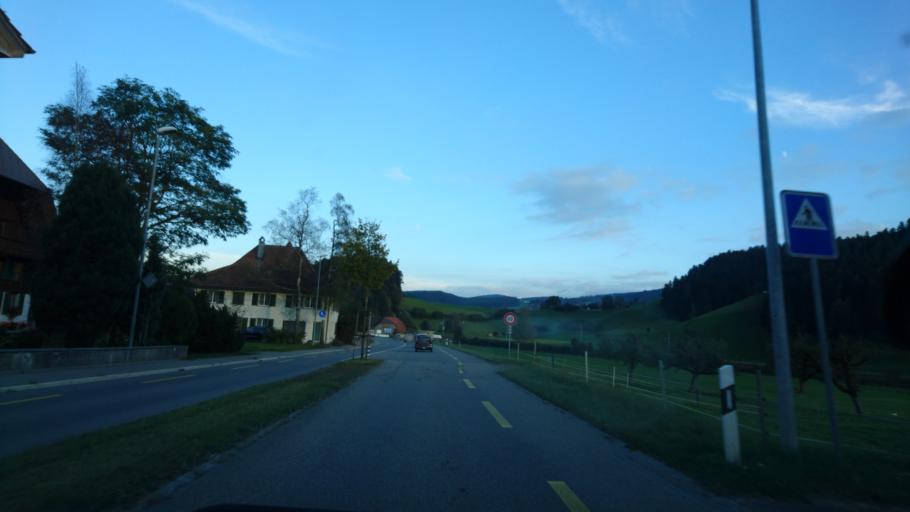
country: CH
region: Bern
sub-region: Bern-Mittelland District
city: Bowil
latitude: 46.9006
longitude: 7.6814
